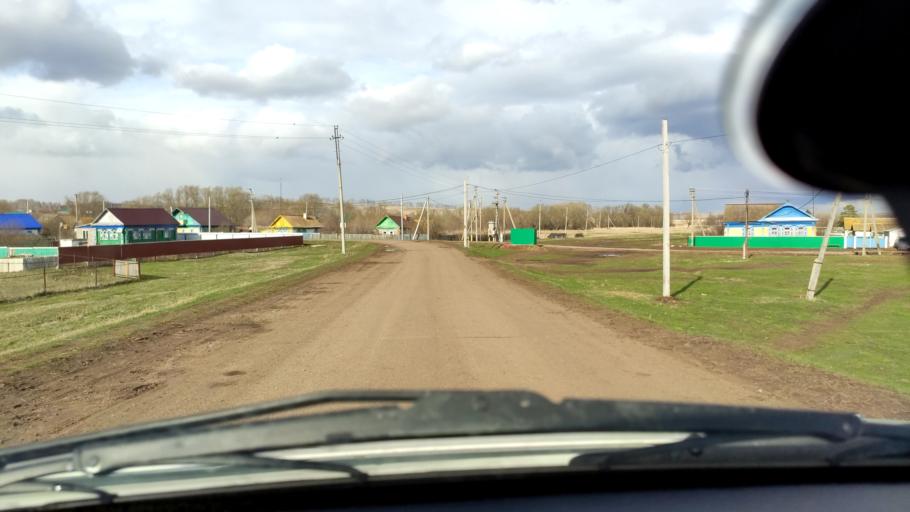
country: RU
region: Bashkortostan
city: Buzdyak
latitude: 54.7685
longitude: 54.6243
